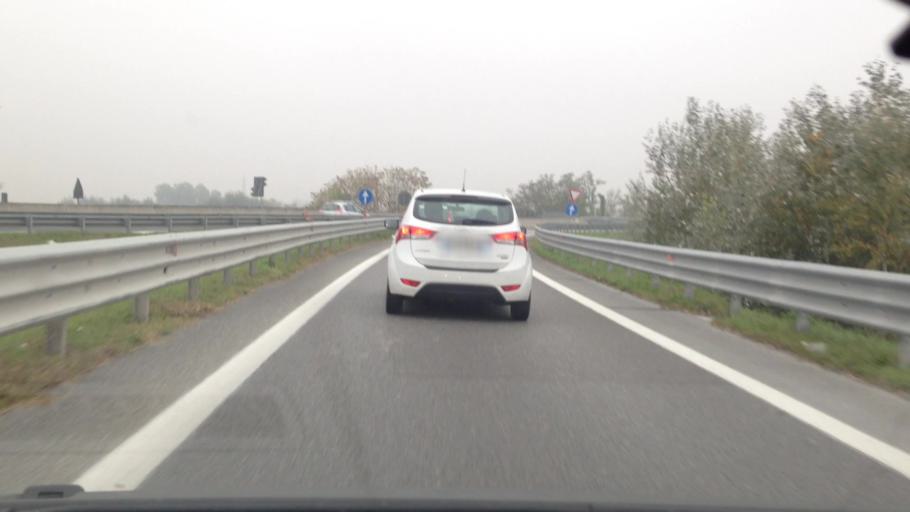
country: IT
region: Piedmont
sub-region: Provincia di Asti
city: Azzano d'Asti
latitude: 44.9046
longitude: 8.2453
